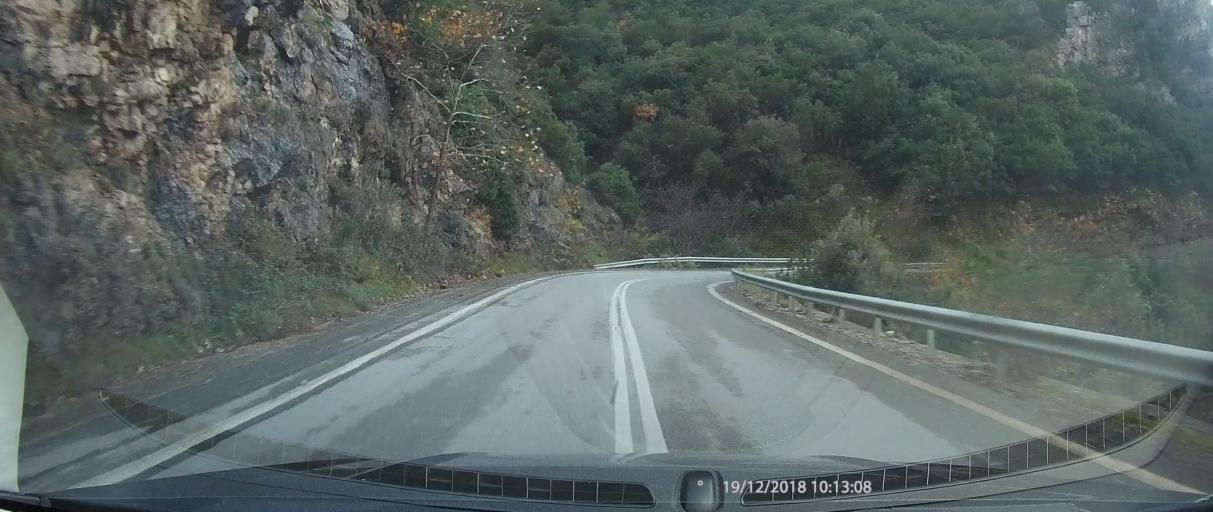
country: GR
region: Peloponnese
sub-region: Nomos Messinias
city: Kalamata
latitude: 37.0870
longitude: 22.1617
